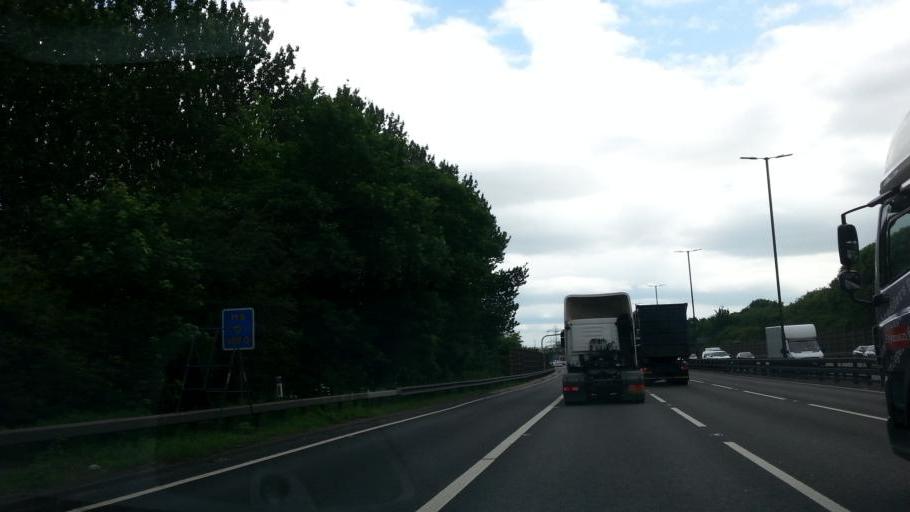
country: GB
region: England
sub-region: City and Borough of Birmingham
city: Hockley
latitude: 52.5324
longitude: -1.8996
